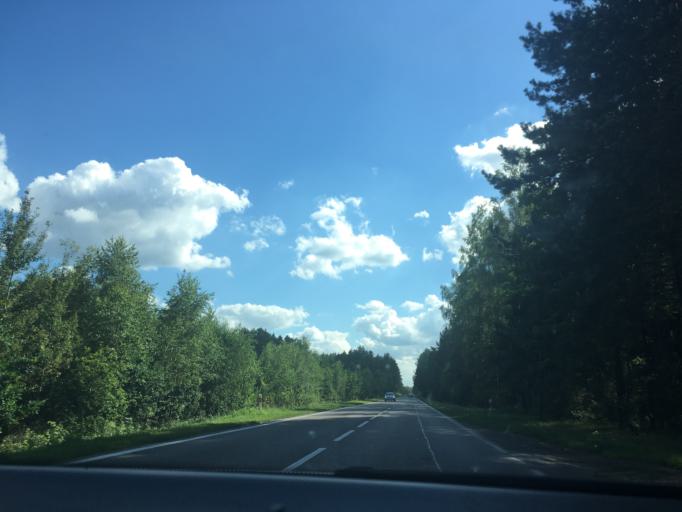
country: PL
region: Podlasie
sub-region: Powiat sokolski
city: Janow
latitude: 53.3587
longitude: 23.1031
